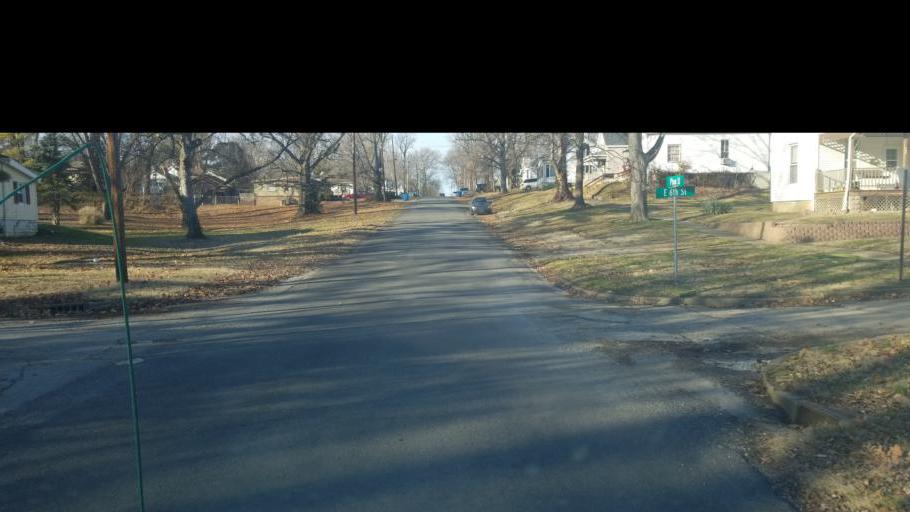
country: US
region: Illinois
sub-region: Wabash County
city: Mount Carmel
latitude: 38.4142
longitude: -87.7560
